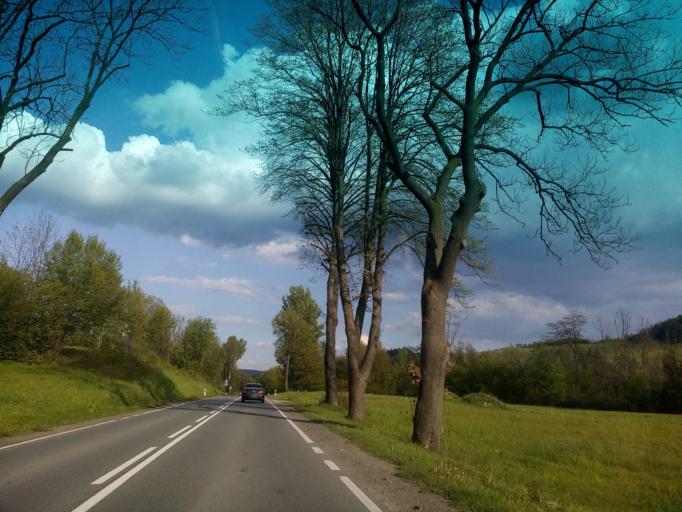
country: PL
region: Lesser Poland Voivodeship
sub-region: Powiat nowosadecki
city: Kamionka Wielka
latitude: 49.5426
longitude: 20.7901
